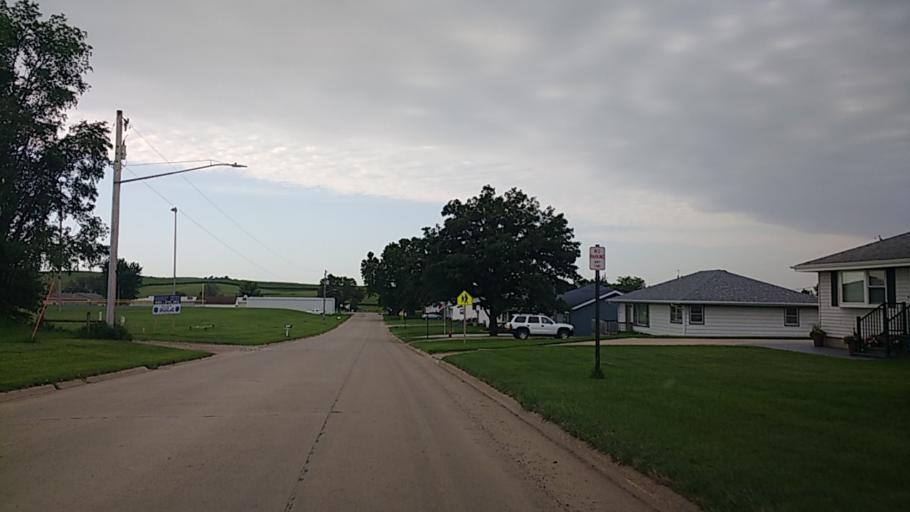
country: US
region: Iowa
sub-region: Woodbury County
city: Moville
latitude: 42.4848
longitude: -96.0653
